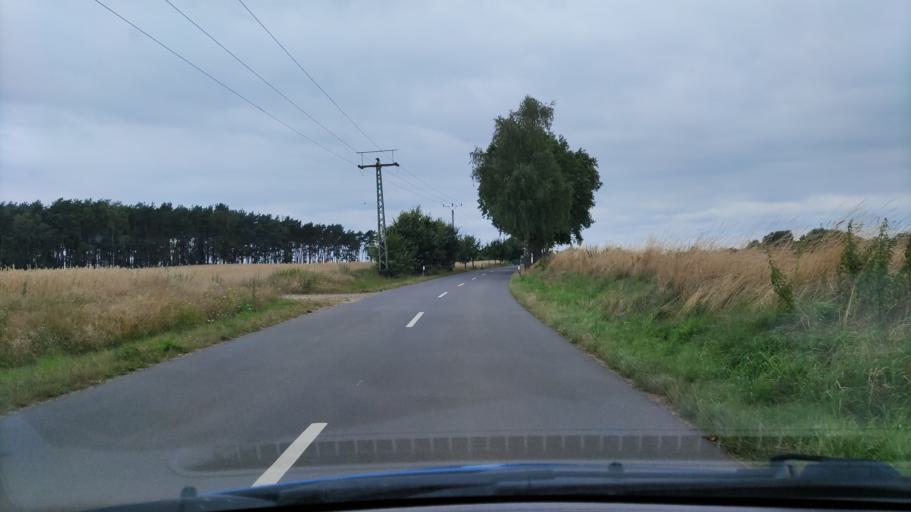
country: DE
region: Lower Saxony
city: Rosche
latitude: 53.0038
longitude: 10.7610
